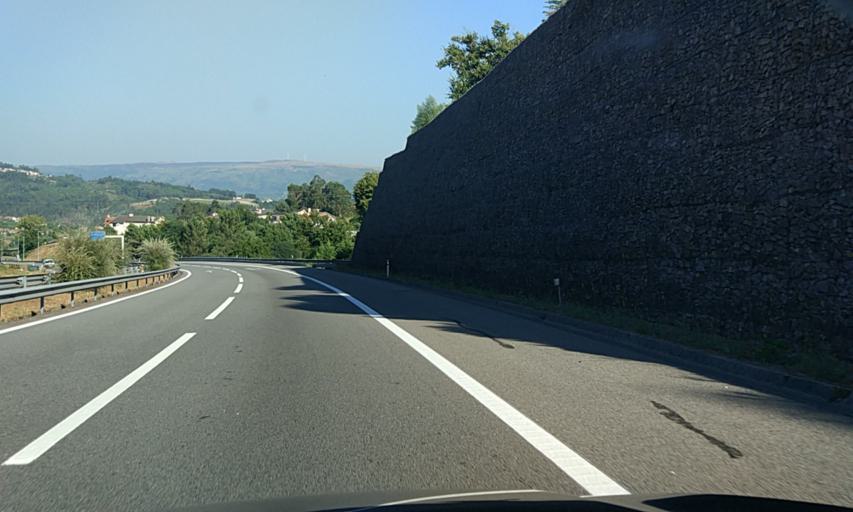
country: PT
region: Porto
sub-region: Marco de Canaveses
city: Marco de Canavezes
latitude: 41.2338
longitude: -8.1904
